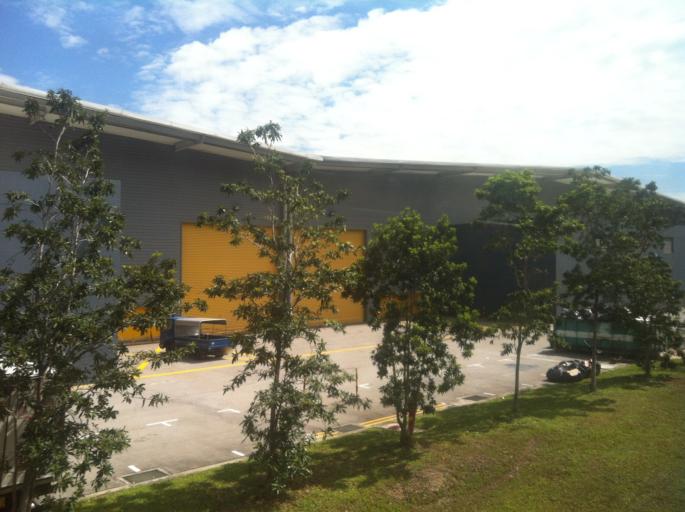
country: SG
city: Singapore
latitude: 1.3367
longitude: 103.9627
